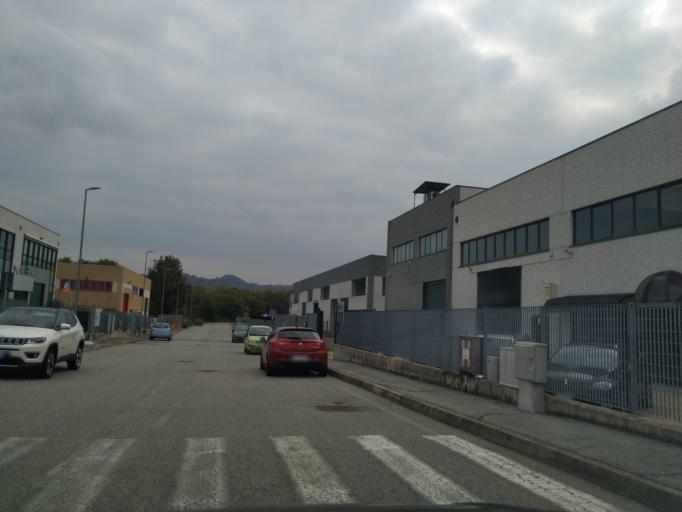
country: IT
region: Piedmont
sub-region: Provincia di Torino
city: Chivasso
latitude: 45.1952
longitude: 7.9187
